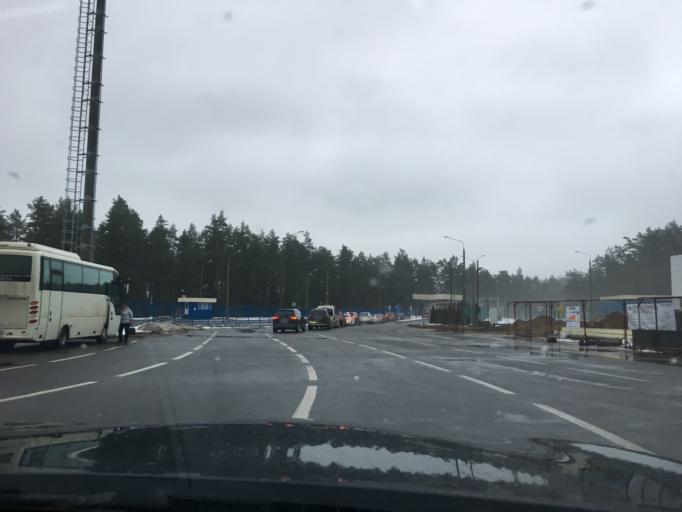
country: LT
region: Alytaus apskritis
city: Druskininkai
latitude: 53.9400
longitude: 23.9667
